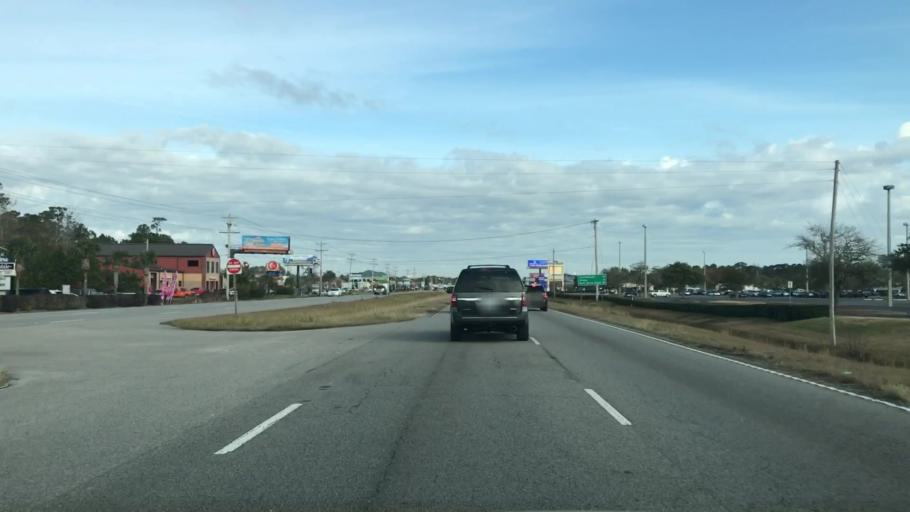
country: US
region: South Carolina
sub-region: Horry County
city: Garden City
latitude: 33.5798
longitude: -79.0283
